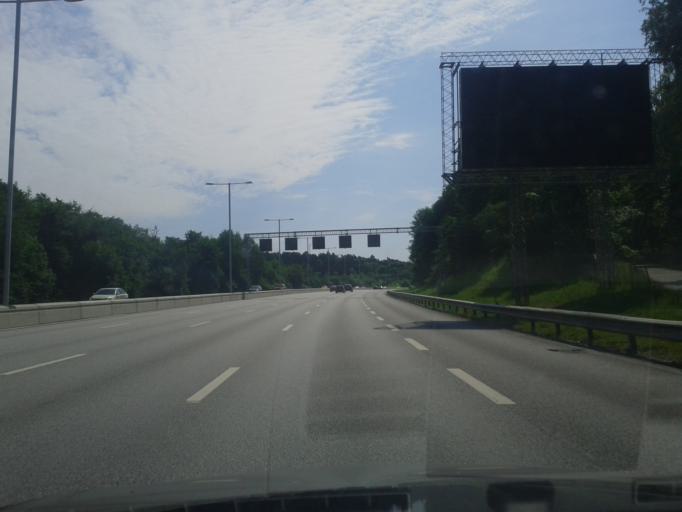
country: SE
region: Stockholm
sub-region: Solna Kommun
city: Rasunda
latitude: 59.3902
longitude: 17.9961
